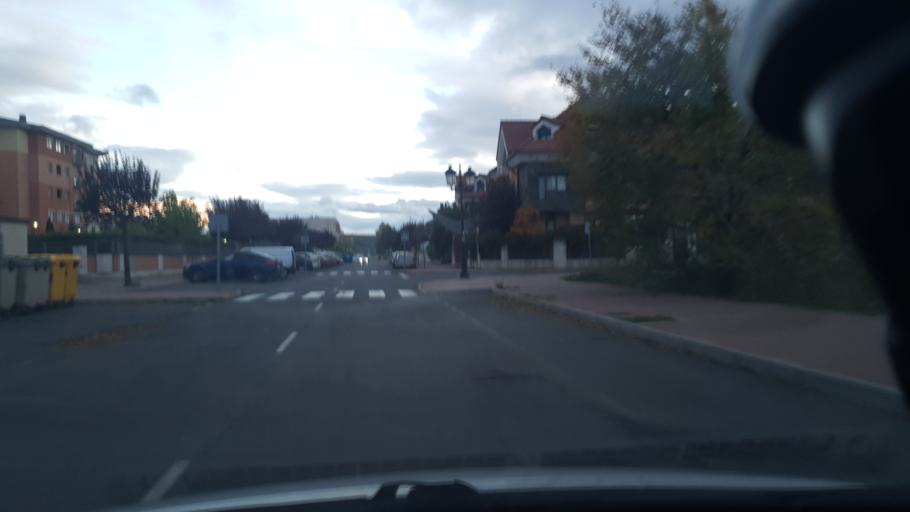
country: ES
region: Castille and Leon
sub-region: Provincia de Avila
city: Avila
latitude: 40.6431
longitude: -4.7004
